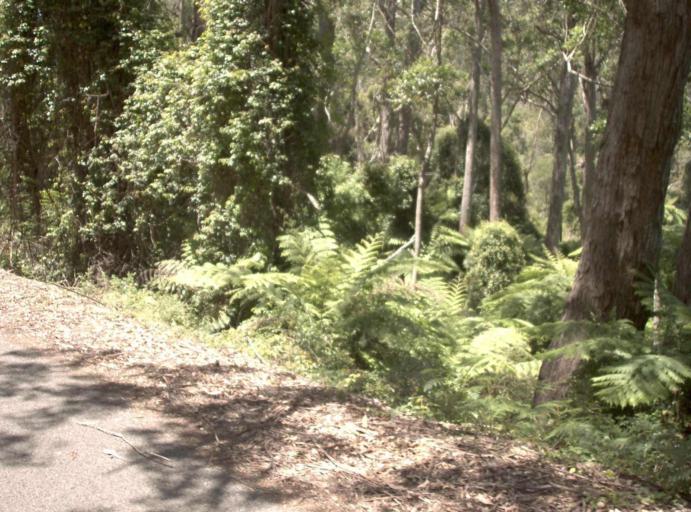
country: AU
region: New South Wales
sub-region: Bombala
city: Bombala
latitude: -37.4508
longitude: 148.9345
